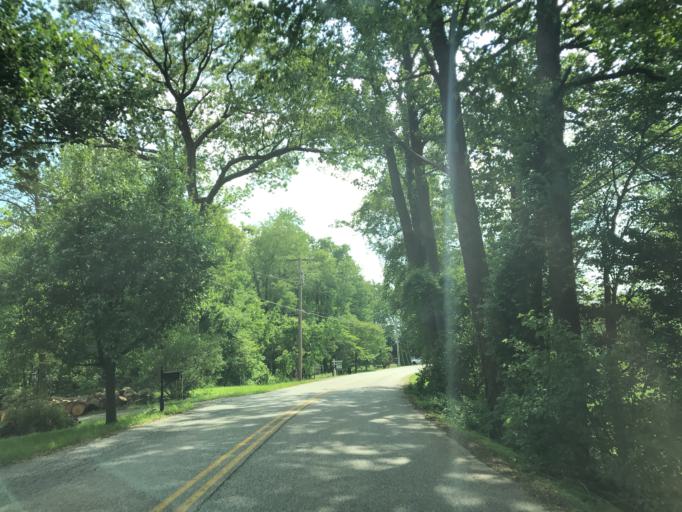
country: US
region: Maryland
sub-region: Harford County
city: Bel Air North
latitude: 39.6111
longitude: -76.3599
